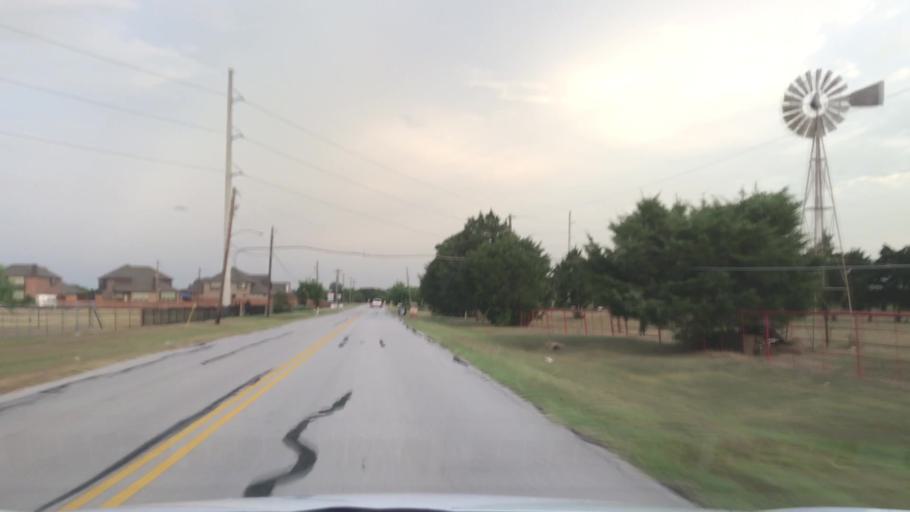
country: US
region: Texas
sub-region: Dallas County
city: Seagoville
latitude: 32.6980
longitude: -96.5595
